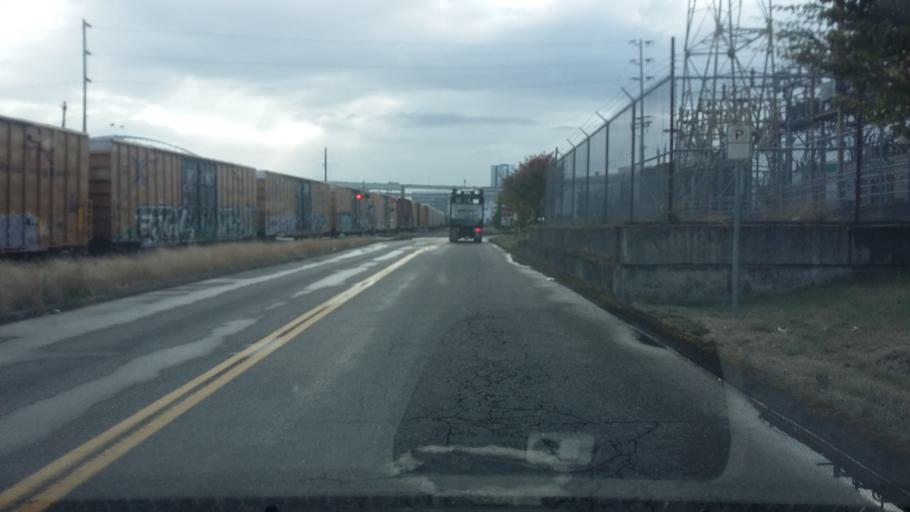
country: US
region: Oregon
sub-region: Multnomah County
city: Portland
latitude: 45.5411
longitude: -122.6959
